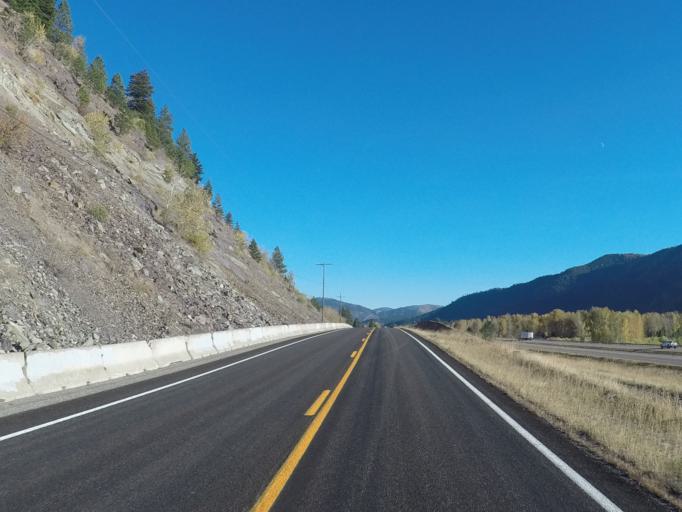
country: US
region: Montana
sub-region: Missoula County
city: Clinton
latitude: 46.8131
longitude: -113.7889
